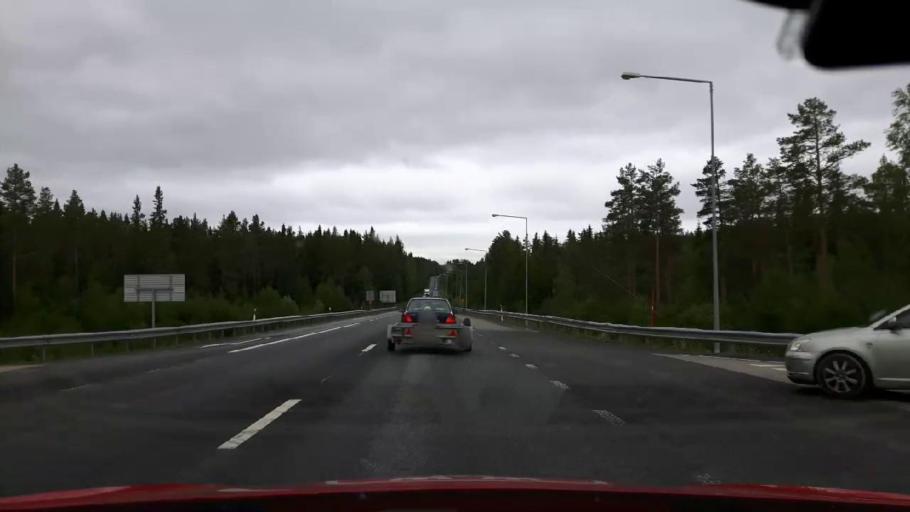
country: SE
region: Jaemtland
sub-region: OEstersunds Kommun
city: Ostersund
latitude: 63.2012
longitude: 14.6746
